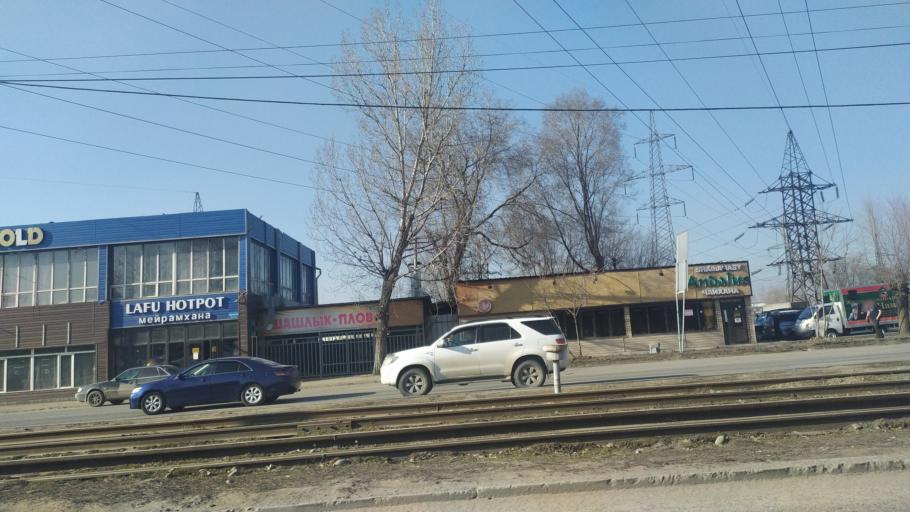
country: KZ
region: Almaty Qalasy
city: Almaty
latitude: 43.2442
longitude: 76.8508
